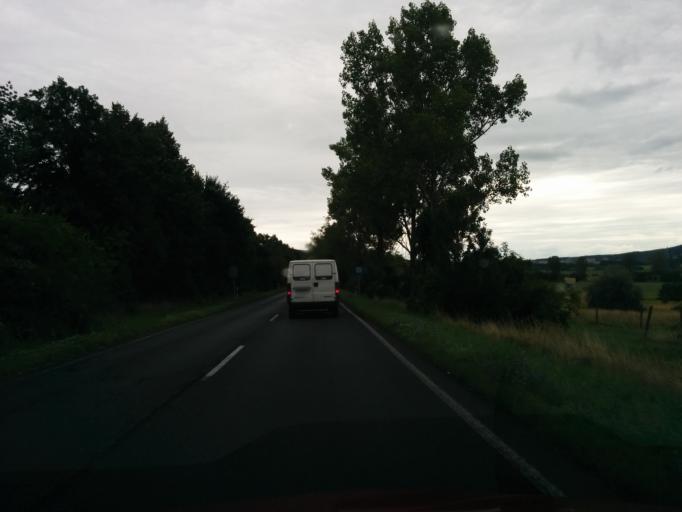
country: AT
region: Burgenland
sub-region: Eisenstadt-Umgebung
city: Klingenbach
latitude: 47.7218
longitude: 16.5644
